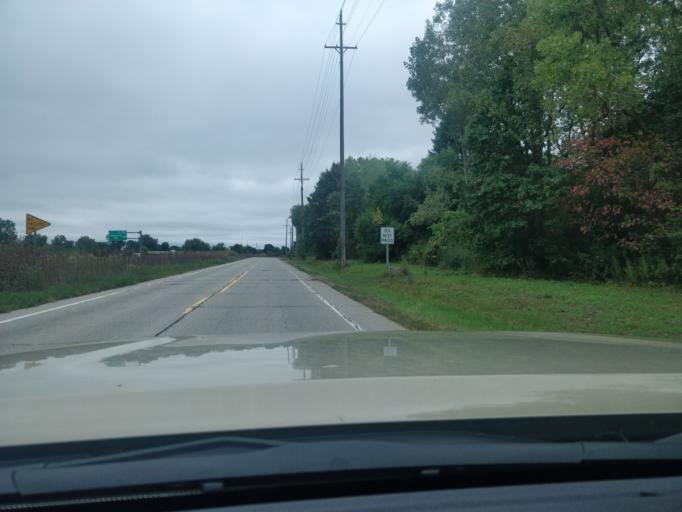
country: US
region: Michigan
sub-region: Wayne County
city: Romulus
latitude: 42.2210
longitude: -83.4319
